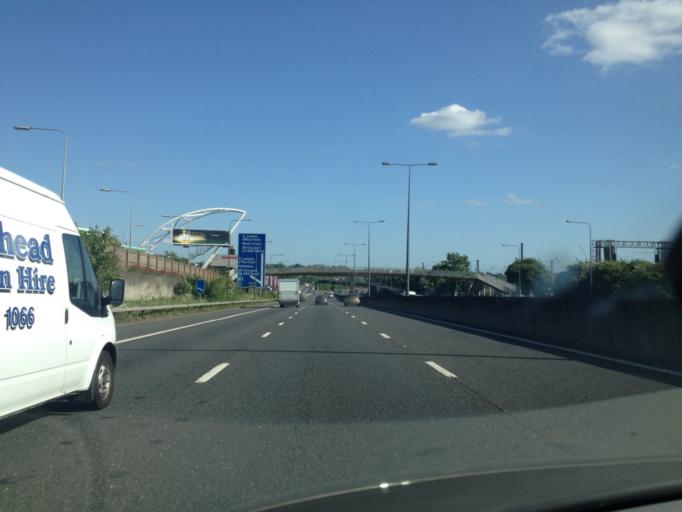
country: GB
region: England
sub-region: Greater London
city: Hendon
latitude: 51.6060
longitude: -0.2415
